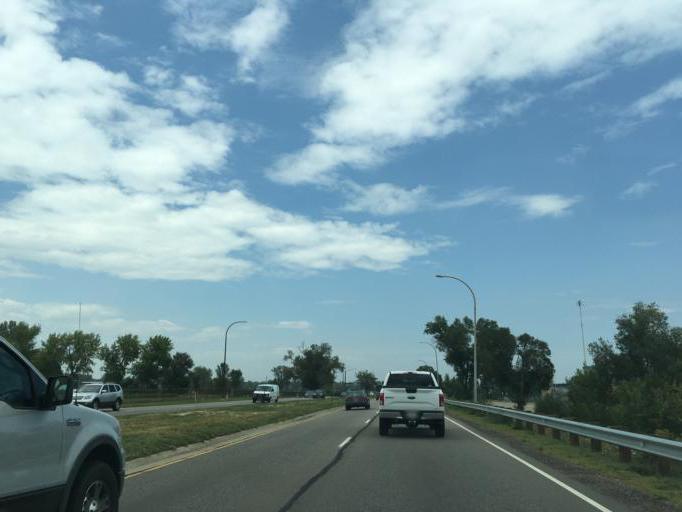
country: US
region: Colorado
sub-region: Jefferson County
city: Lakewood
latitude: 39.7197
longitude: -105.1097
